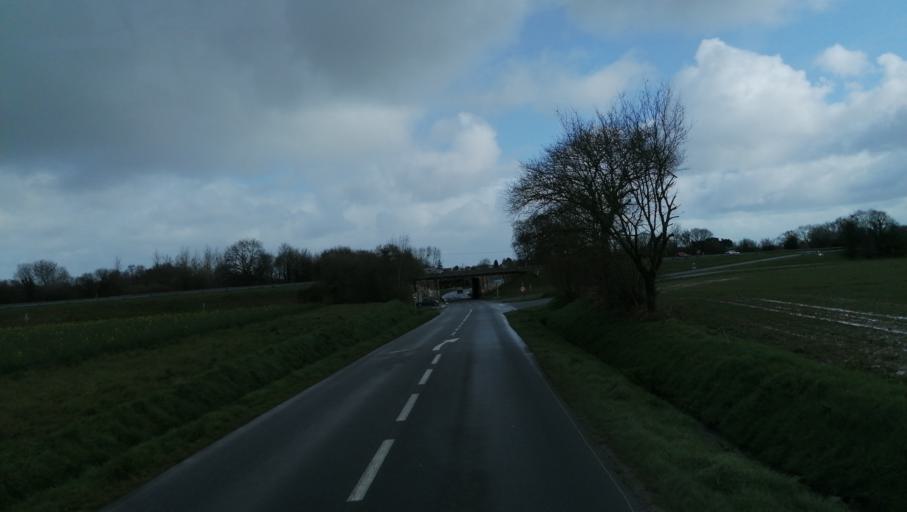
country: FR
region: Brittany
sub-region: Departement des Cotes-d'Armor
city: Plouagat
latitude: 48.5320
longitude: -3.0097
